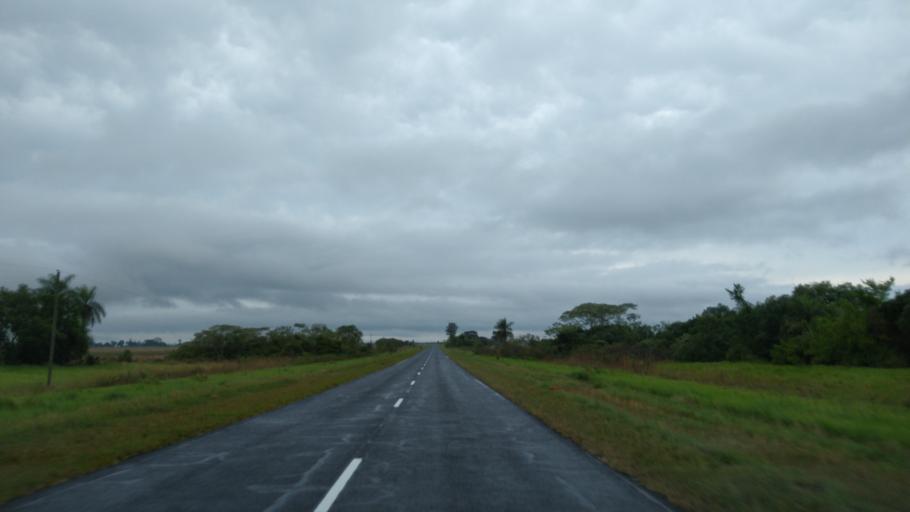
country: AR
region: Corrientes
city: Loreto
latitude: -27.7267
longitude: -57.2381
